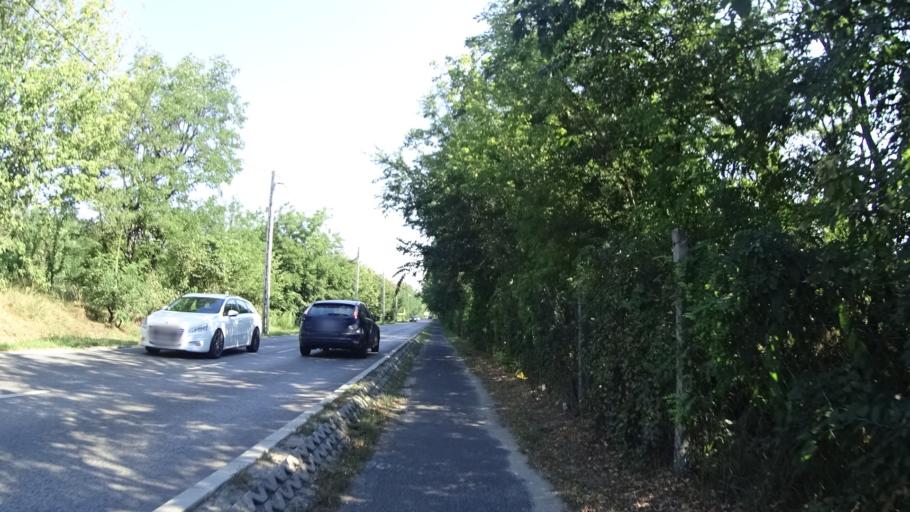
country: HU
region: Pest
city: Dunakeszi
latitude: 47.6128
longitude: 19.1313
